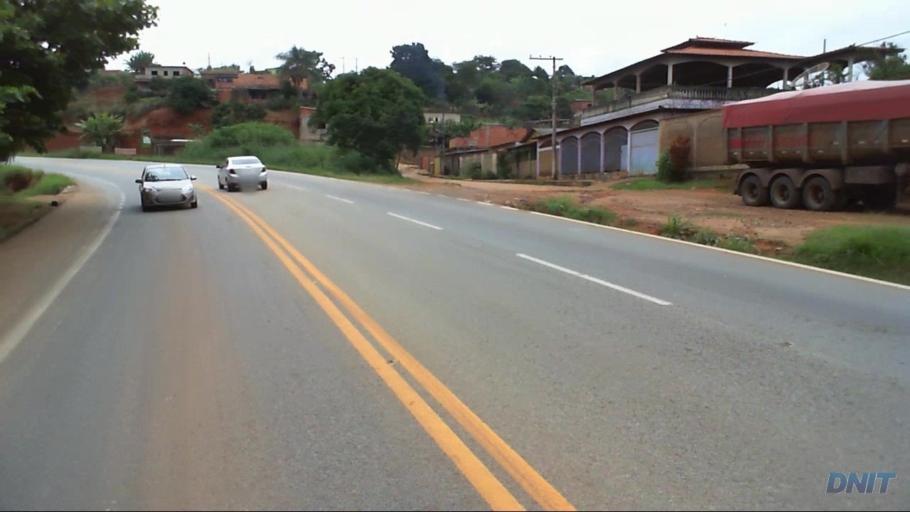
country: BR
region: Minas Gerais
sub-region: Nova Era
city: Nova Era
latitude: -19.8170
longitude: -43.0667
